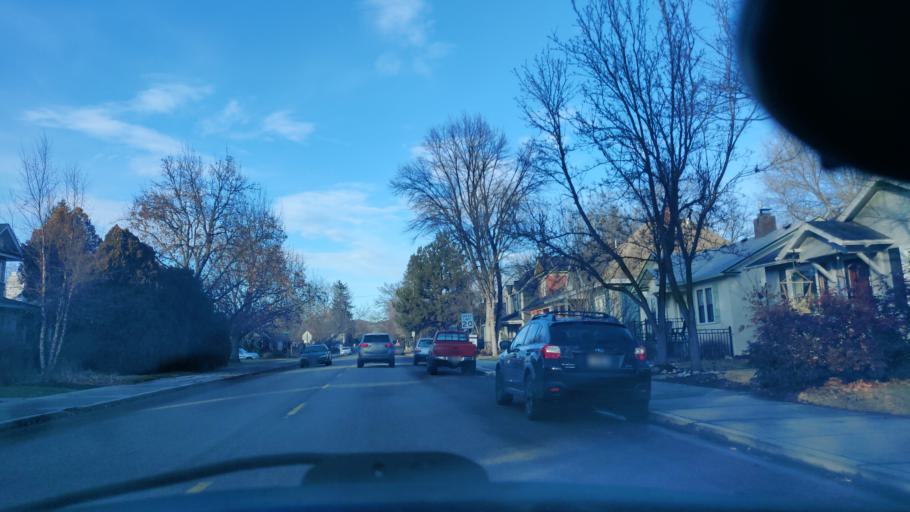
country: US
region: Idaho
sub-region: Ada County
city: Boise
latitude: 43.6267
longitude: -116.2034
